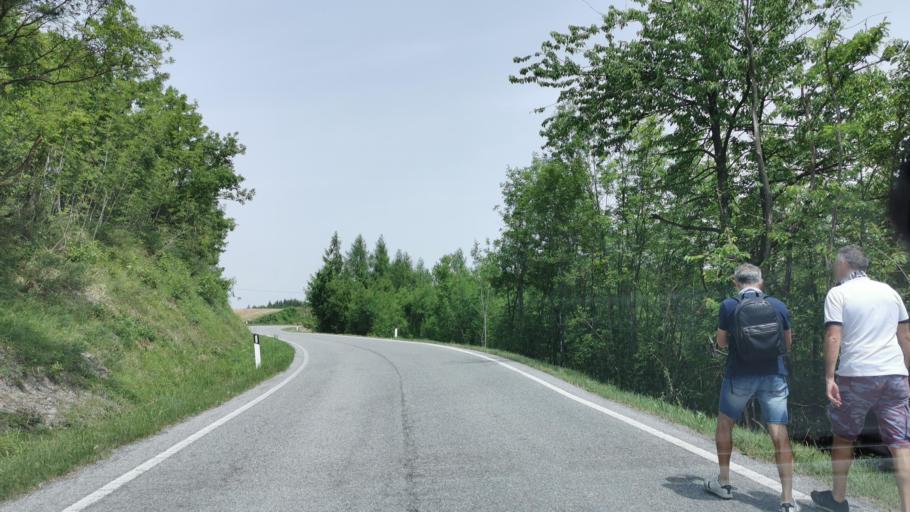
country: IT
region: Piedmont
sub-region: Provincia di Cuneo
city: Sale San Giovanni
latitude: 44.4071
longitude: 8.0772
